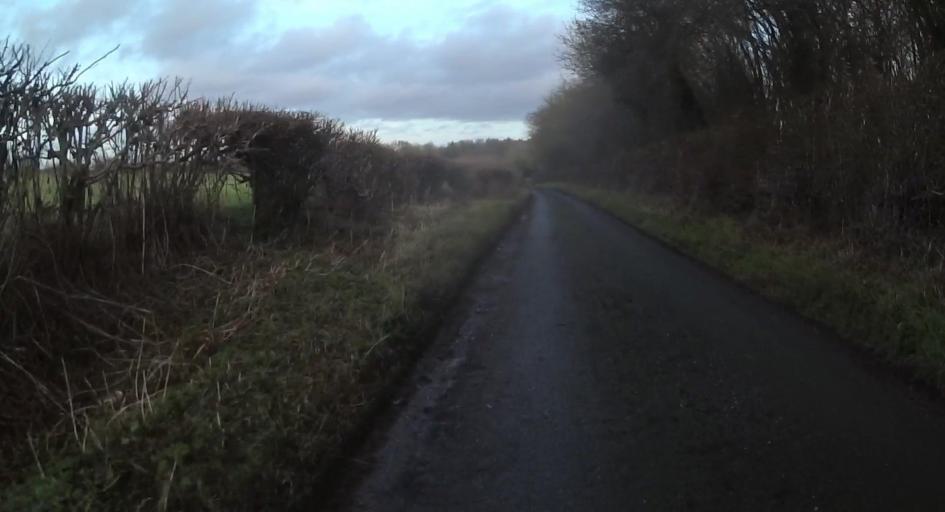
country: GB
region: England
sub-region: Hampshire
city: Long Sutton
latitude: 51.2302
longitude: -0.9300
